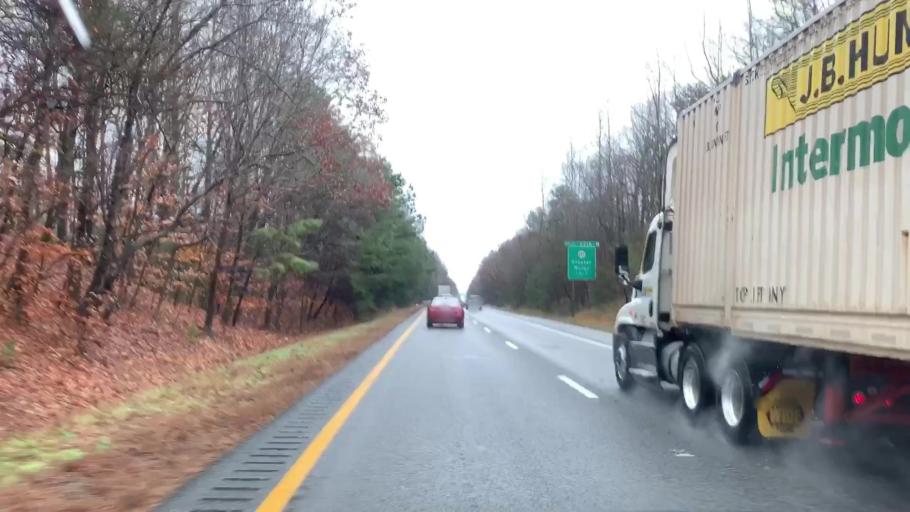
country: US
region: Virginia
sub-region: James City County
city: Williamsburg
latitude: 37.3995
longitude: -76.7790
